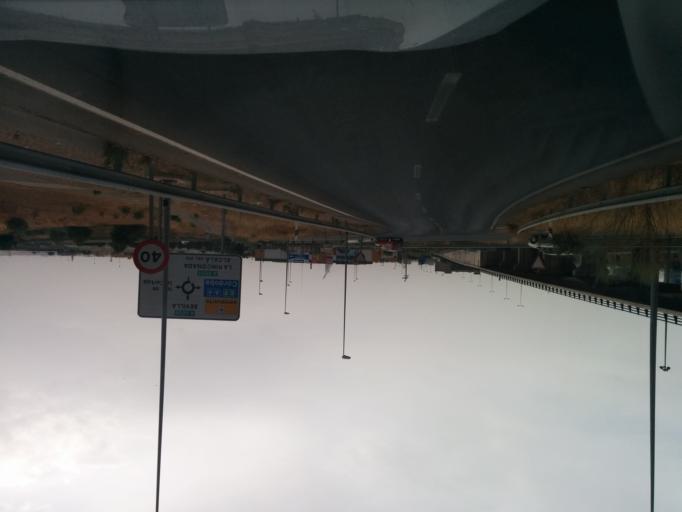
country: ES
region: Andalusia
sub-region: Provincia de Sevilla
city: La Algaba
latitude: 37.4371
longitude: -5.9731
